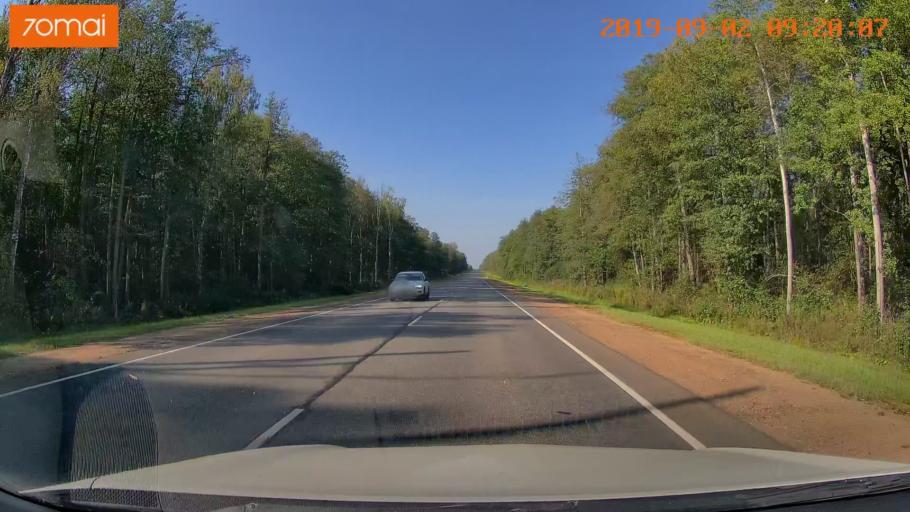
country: RU
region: Kaluga
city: Yukhnov
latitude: 54.8031
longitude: 35.3913
